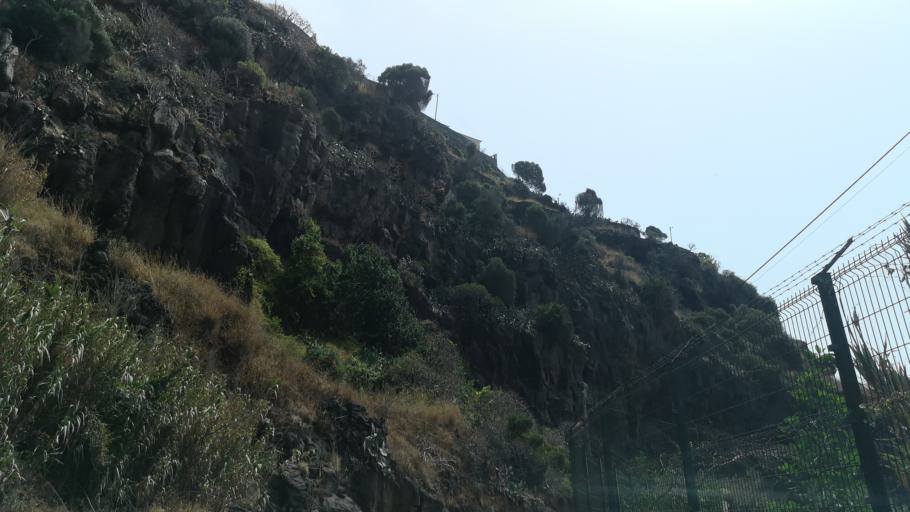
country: PT
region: Madeira
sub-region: Santa Cruz
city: Santa Cruz
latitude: 32.6628
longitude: -16.8104
